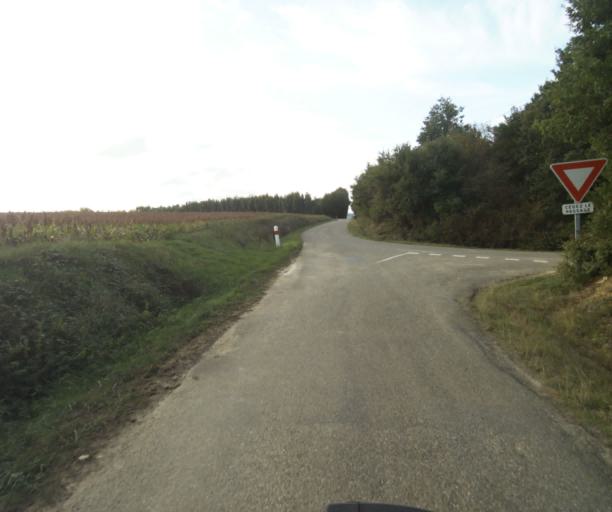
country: FR
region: Midi-Pyrenees
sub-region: Departement de la Haute-Garonne
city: Launac
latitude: 43.8140
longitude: 1.0966
